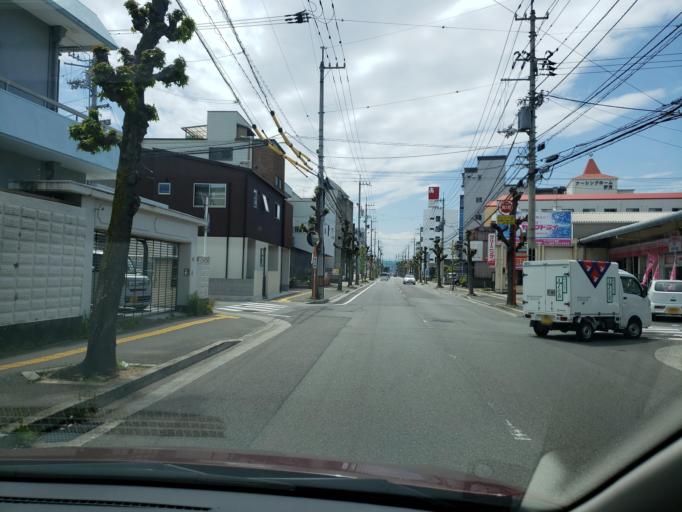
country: JP
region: Tokushima
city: Tokushima-shi
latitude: 34.0647
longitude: 134.5717
